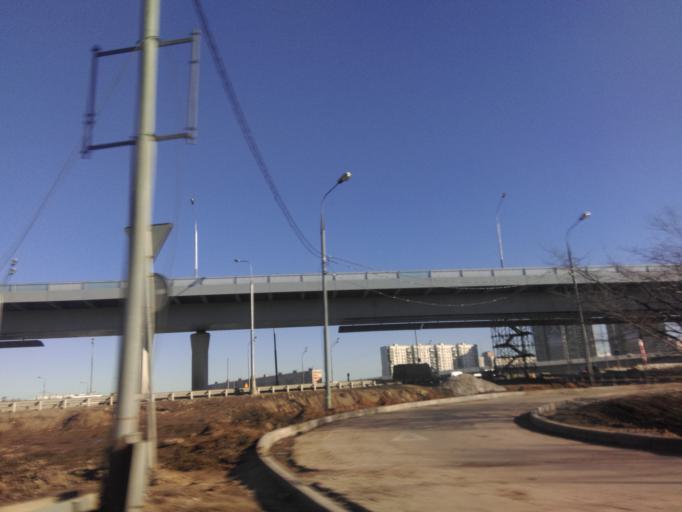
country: RU
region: Moskovskaya
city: Marfino
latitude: 55.7126
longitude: 37.3835
